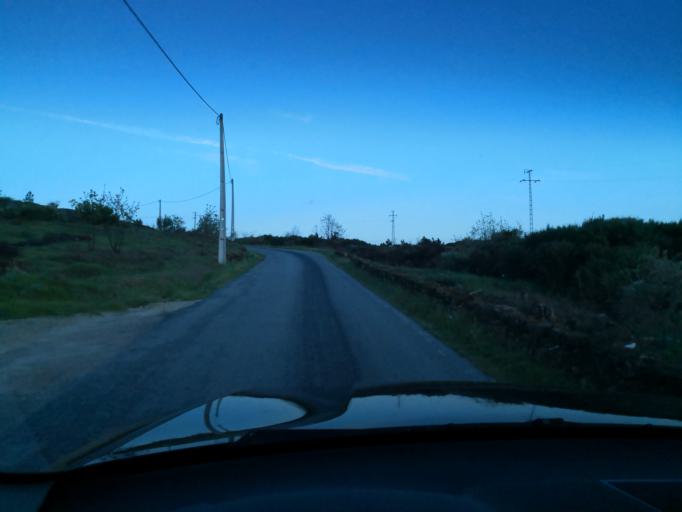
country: PT
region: Vila Real
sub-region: Vila Real
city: Vila Real
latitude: 41.3521
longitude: -7.6731
